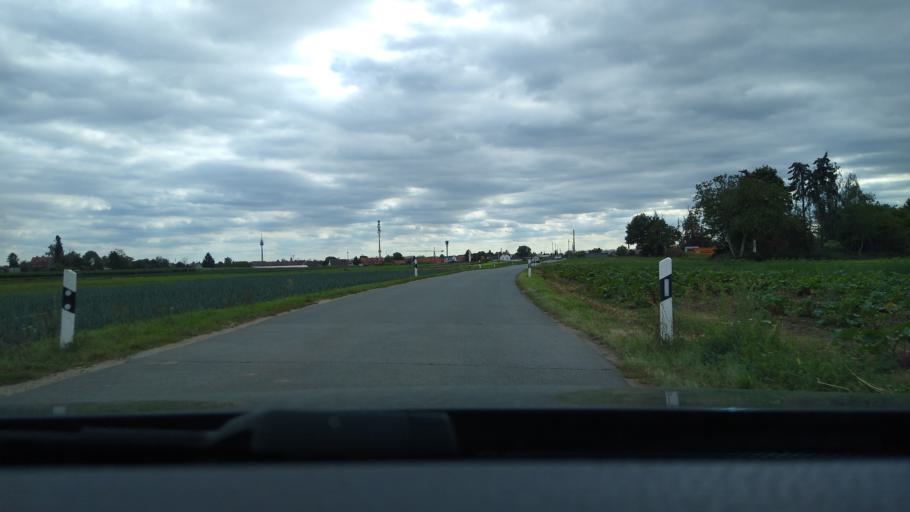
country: DE
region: Bavaria
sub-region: Regierungsbezirk Mittelfranken
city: Wetzendorf
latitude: 49.4790
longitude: 11.0409
